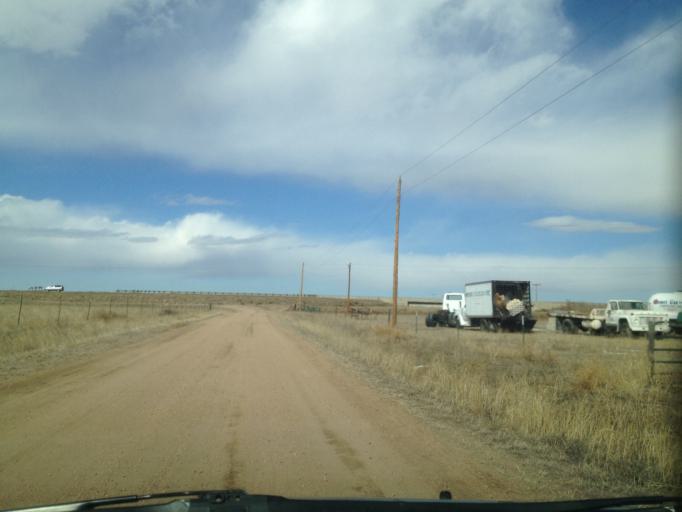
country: US
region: Colorado
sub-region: Weld County
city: Keenesburg
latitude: 40.2895
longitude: -104.2555
